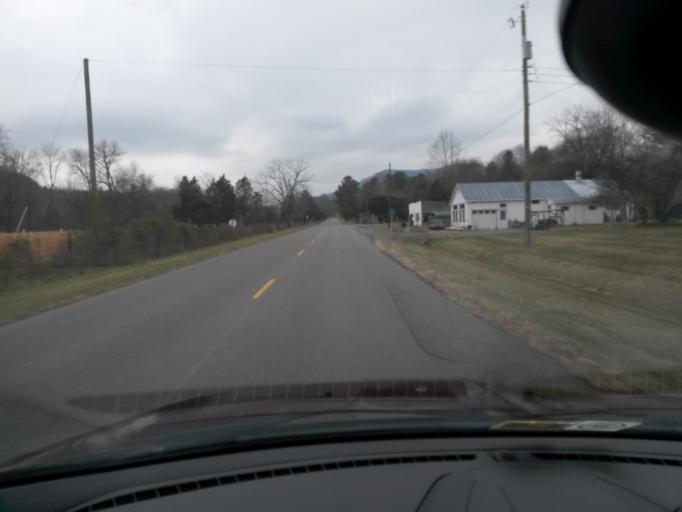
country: US
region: Virginia
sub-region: City of Lexington
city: Lexington
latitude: 37.8534
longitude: -79.4945
